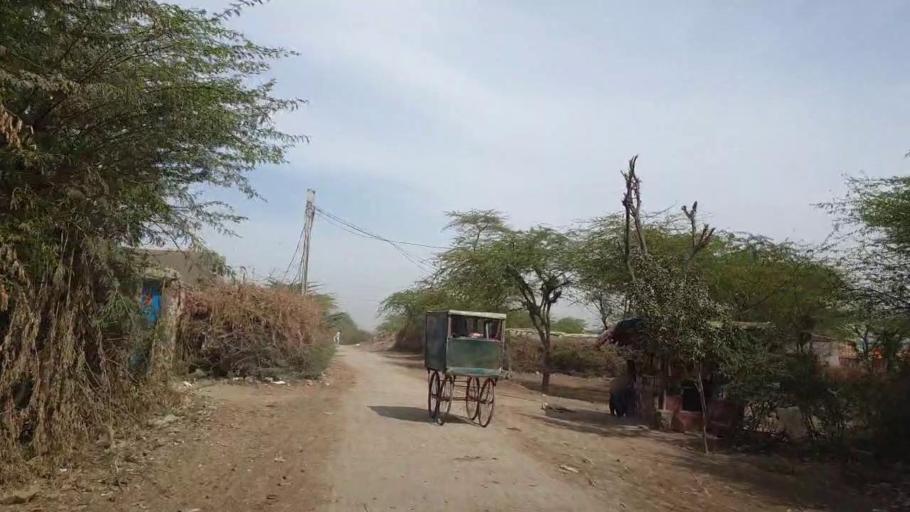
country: PK
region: Sindh
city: Kunri
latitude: 25.1717
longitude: 69.5915
